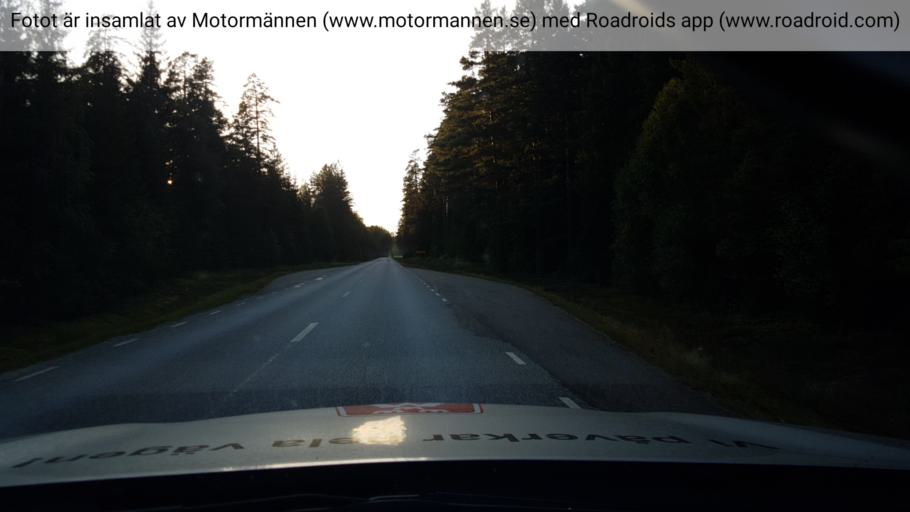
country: SE
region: Dalarna
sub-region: Smedjebackens Kommun
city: Smedjebacken
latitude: 59.9134
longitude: 15.4599
